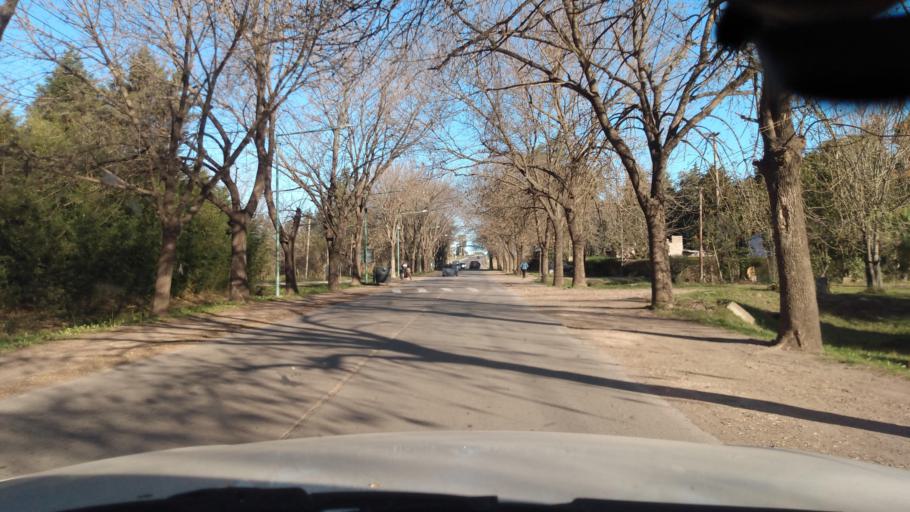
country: AR
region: Buenos Aires
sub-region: Partido de Lujan
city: Lujan
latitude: -34.6285
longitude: -59.2518
